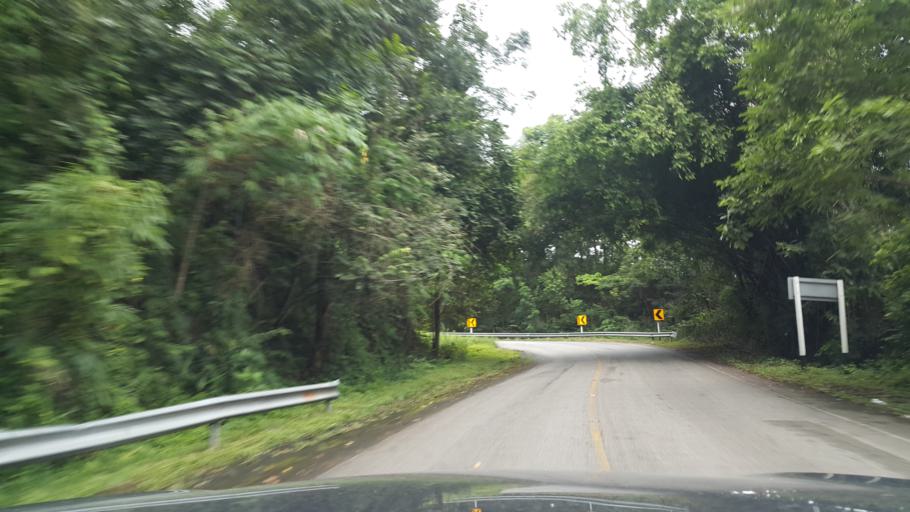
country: TH
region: Chiang Mai
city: Samoeng
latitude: 18.8077
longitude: 98.8115
